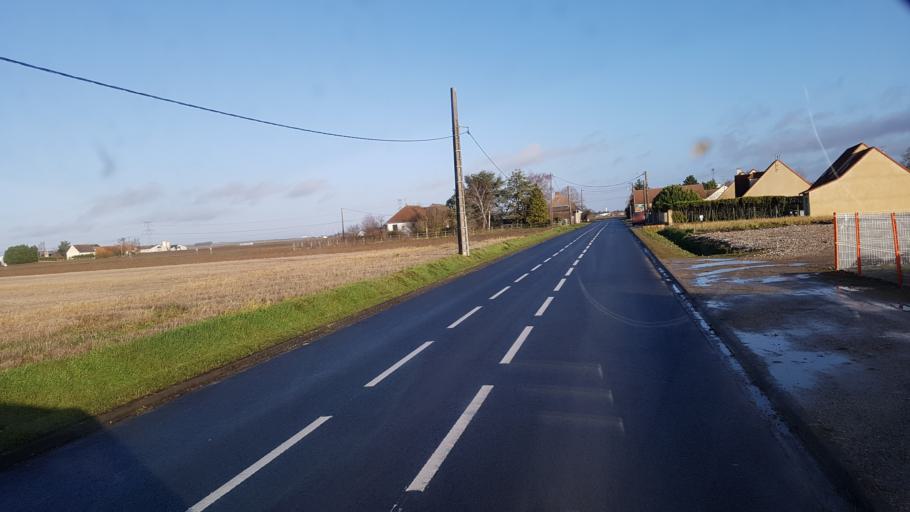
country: FR
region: Centre
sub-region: Departement du Loiret
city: Dadonville
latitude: 48.1043
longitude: 2.2452
